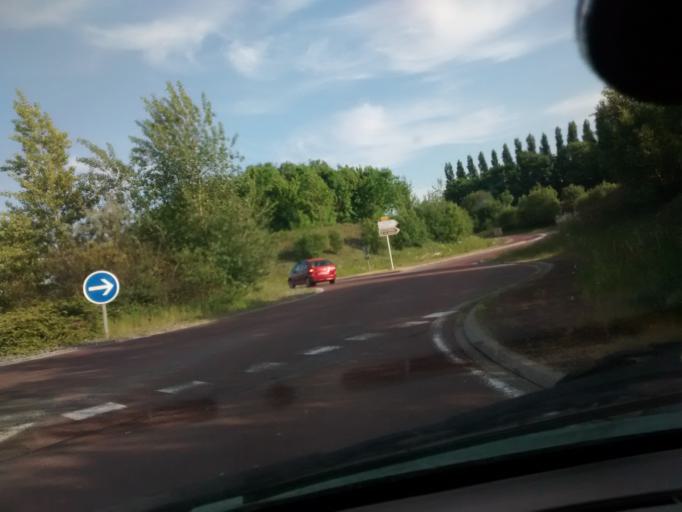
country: FR
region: Lower Normandy
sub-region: Departement de la Manche
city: Pont-Hebert
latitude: 49.1366
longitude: -1.1782
